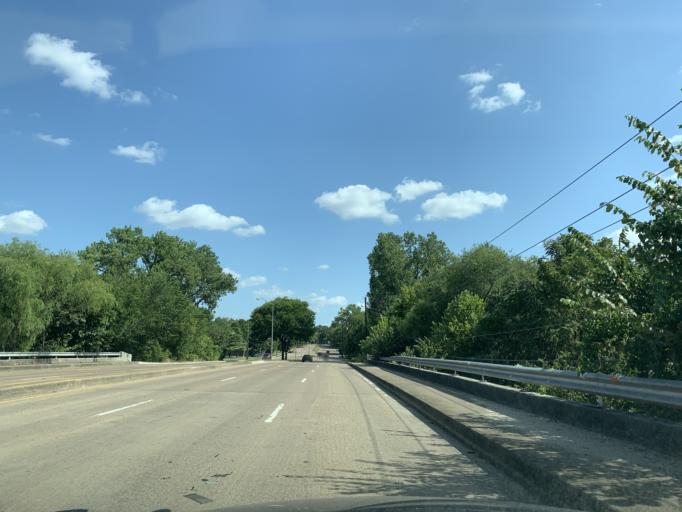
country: US
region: Texas
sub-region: Dallas County
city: Hutchins
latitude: 32.6831
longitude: -96.7679
